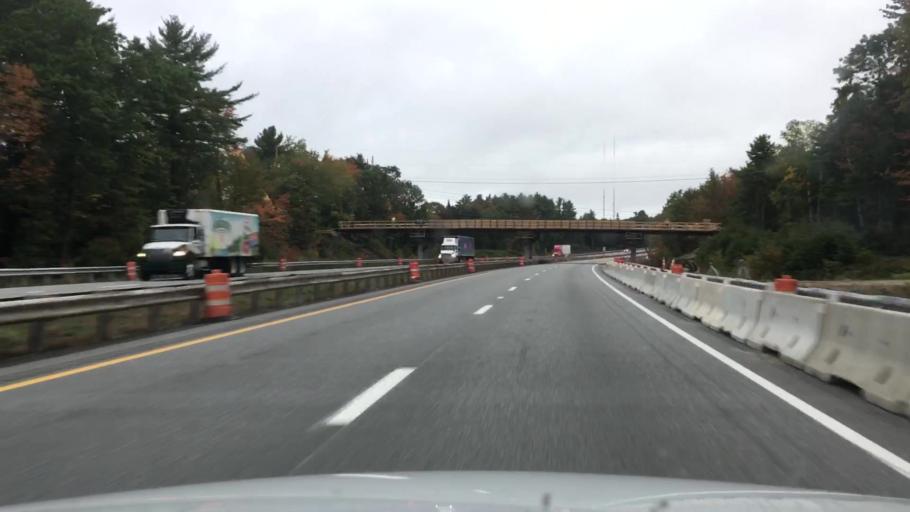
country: US
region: Maine
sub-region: Cumberland County
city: Cumberland Center
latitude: 43.8361
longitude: -70.3242
